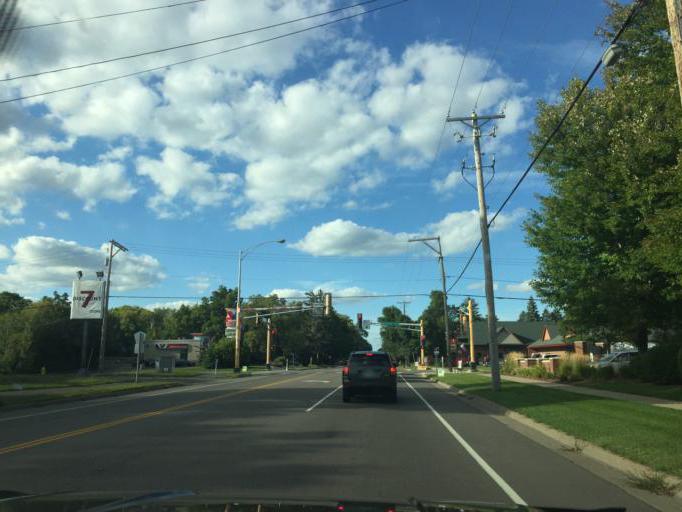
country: US
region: Minnesota
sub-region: Ramsey County
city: Roseville
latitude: 44.9986
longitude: -93.1463
